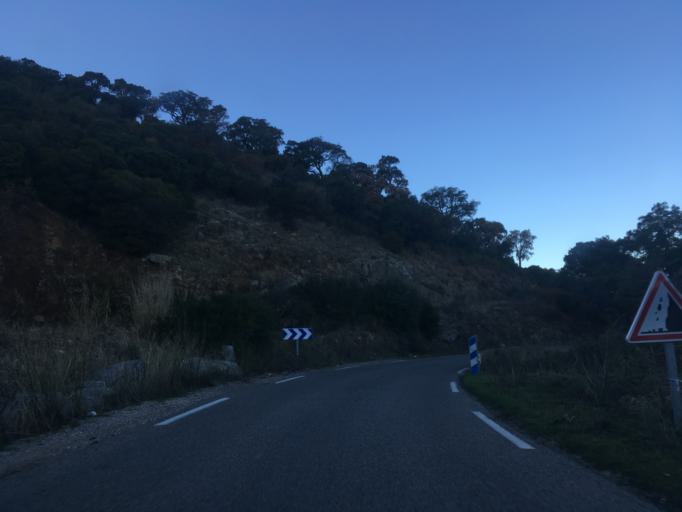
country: FR
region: Provence-Alpes-Cote d'Azur
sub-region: Departement du Var
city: Le Plan-de-la-Tour
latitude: 43.3011
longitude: 6.5568
